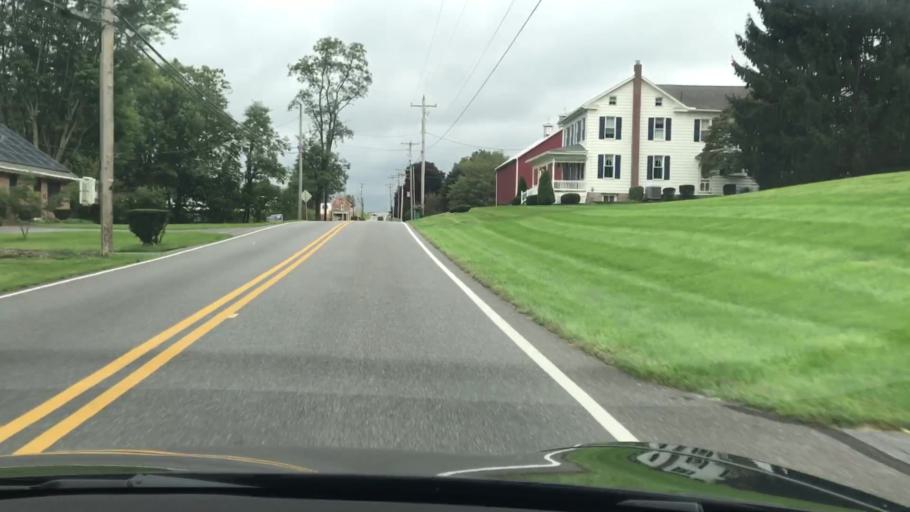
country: US
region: Pennsylvania
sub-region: York County
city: Dillsburg
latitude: 40.1005
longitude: -77.0603
